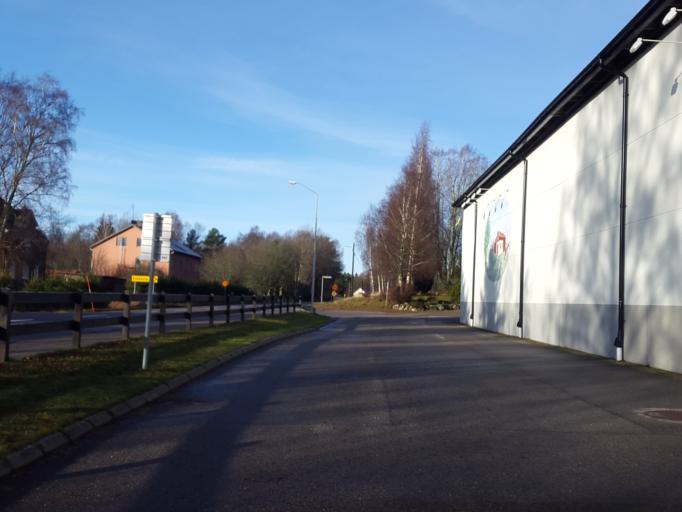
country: SE
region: Vaestra Goetaland
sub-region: Herrljunga Kommun
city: Herrljunga
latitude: 57.9896
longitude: 13.0570
